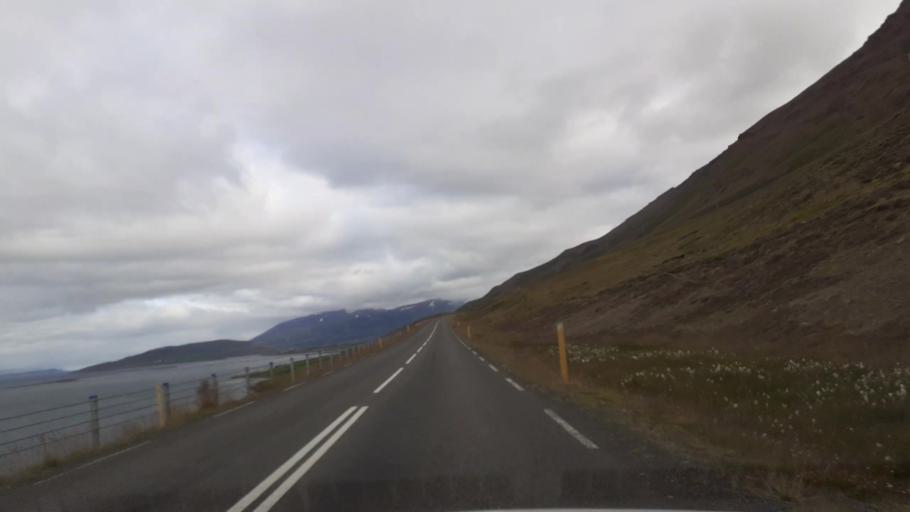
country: IS
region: Northeast
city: Akureyri
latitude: 65.8446
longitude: -18.0580
